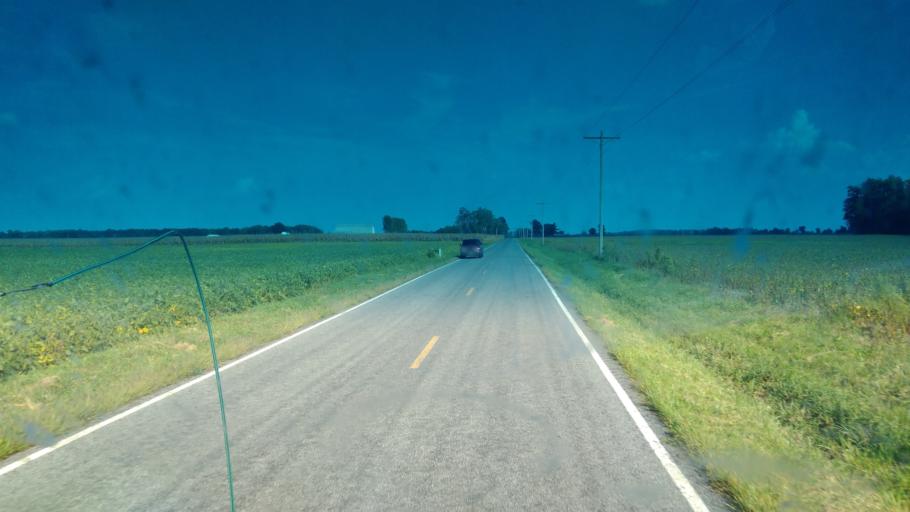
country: US
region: Ohio
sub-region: Hardin County
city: Forest
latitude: 40.9051
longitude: -83.5123
